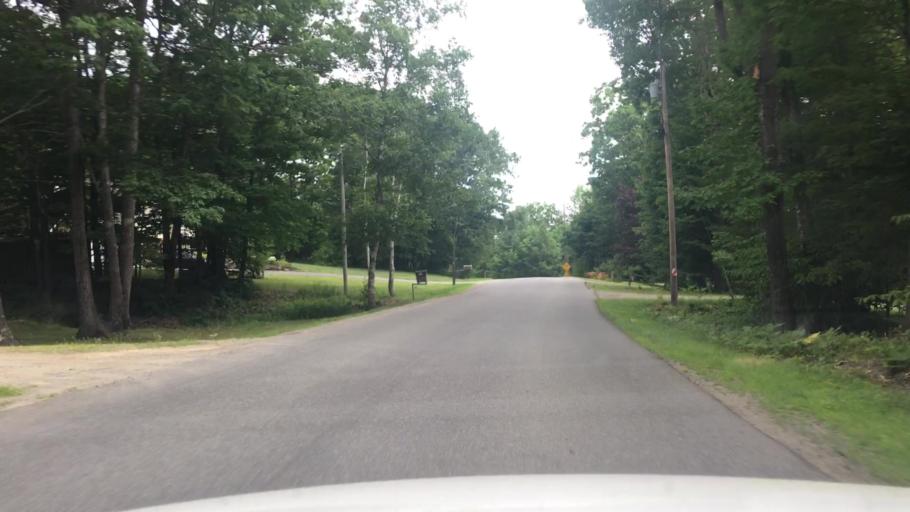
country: US
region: Maine
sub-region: Kennebec County
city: Clinton
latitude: 44.5913
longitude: -69.4709
